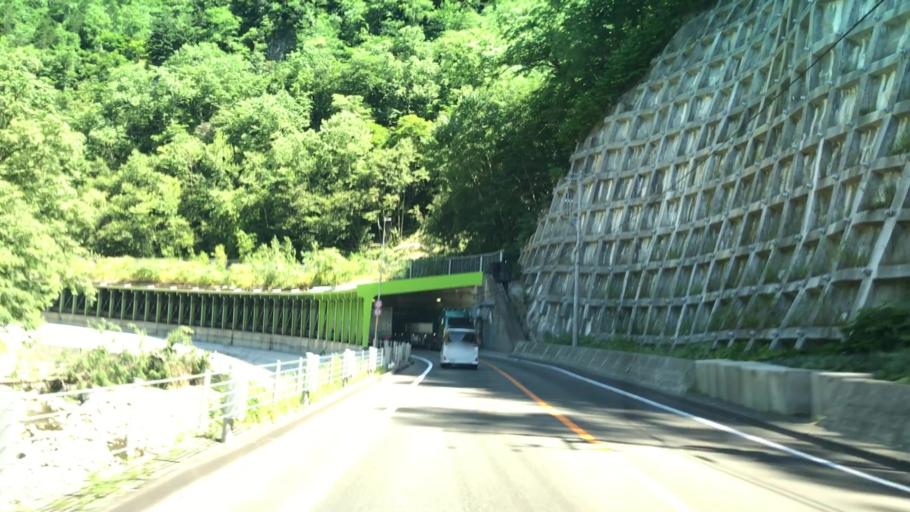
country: JP
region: Hokkaido
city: Shimo-furano
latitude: 42.9375
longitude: 142.6016
